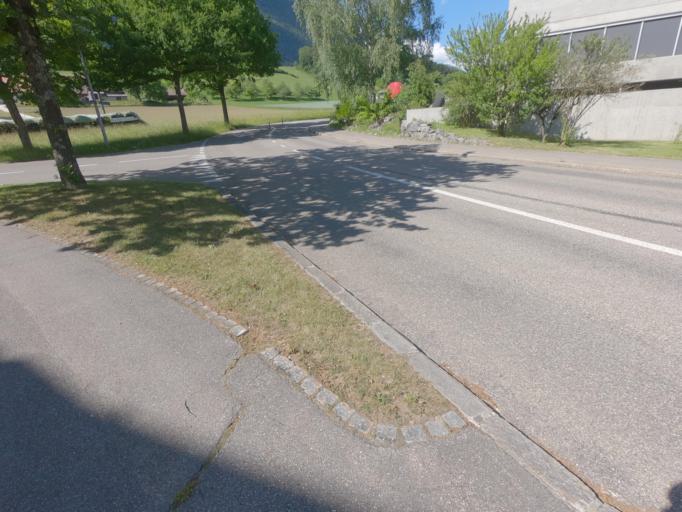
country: CH
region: Solothurn
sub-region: Bezirk Lebern
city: Langendorf
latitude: 47.2332
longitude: 7.5327
